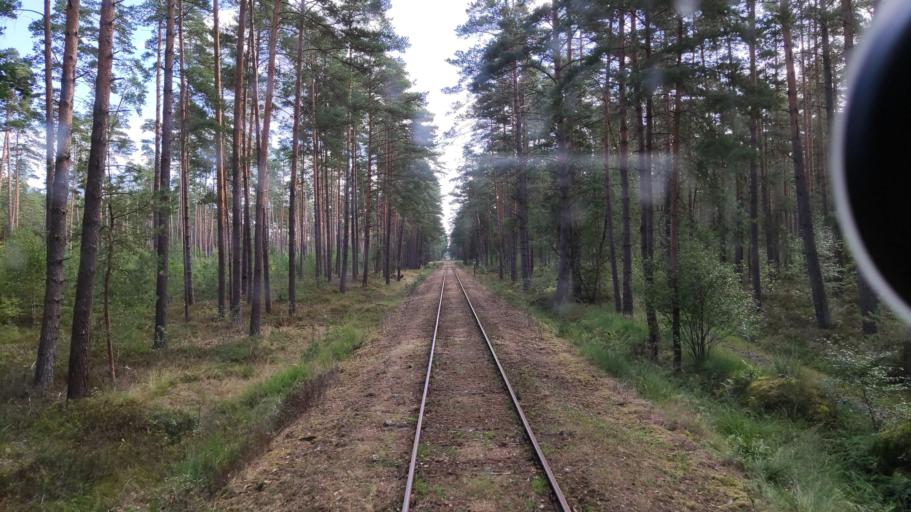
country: DE
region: Lower Saxony
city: Neetze
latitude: 53.2863
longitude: 10.6652
